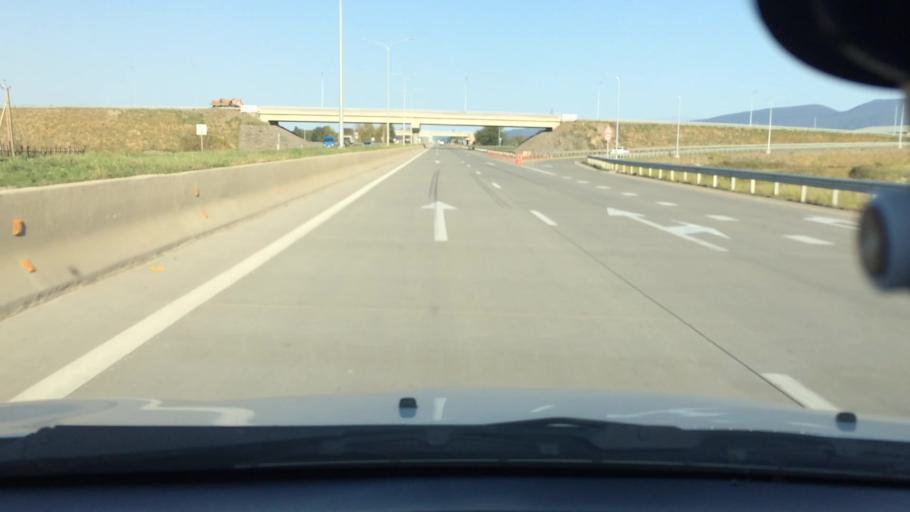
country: GE
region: Imereti
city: Zestap'oni
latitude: 42.1578
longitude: 42.9520
